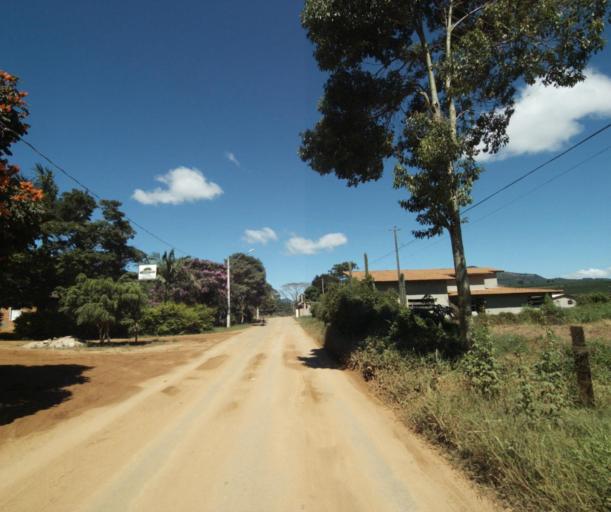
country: BR
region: Minas Gerais
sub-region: Espera Feliz
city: Espera Feliz
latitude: -20.5579
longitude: -41.8207
